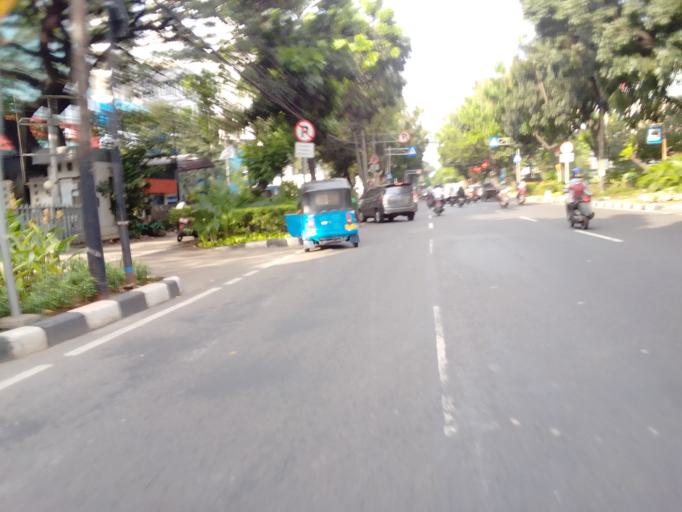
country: ID
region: Jakarta Raya
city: Jakarta
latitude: -6.1831
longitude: 106.8264
